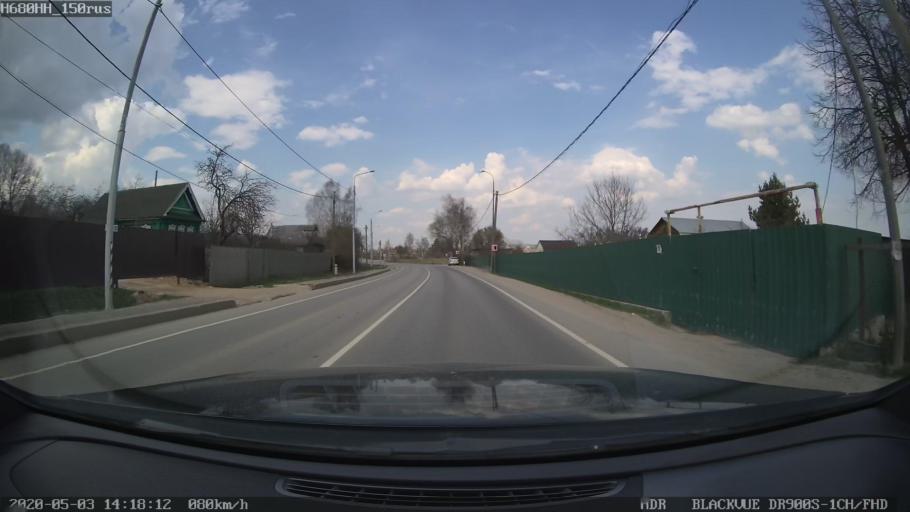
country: RU
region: Moskovskaya
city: Solnechnogorsk
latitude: 56.2159
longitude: 36.9731
